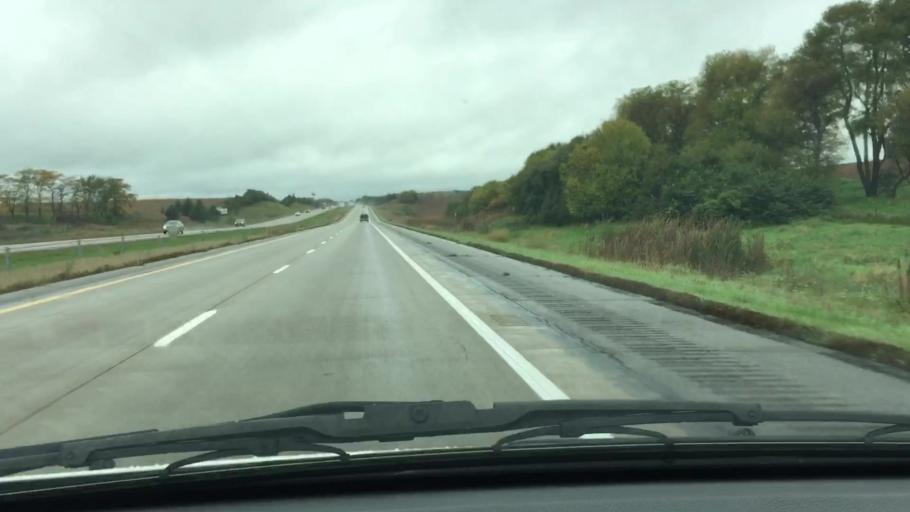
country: US
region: Iowa
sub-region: Jasper County
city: Newton
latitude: 41.6809
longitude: -92.9584
